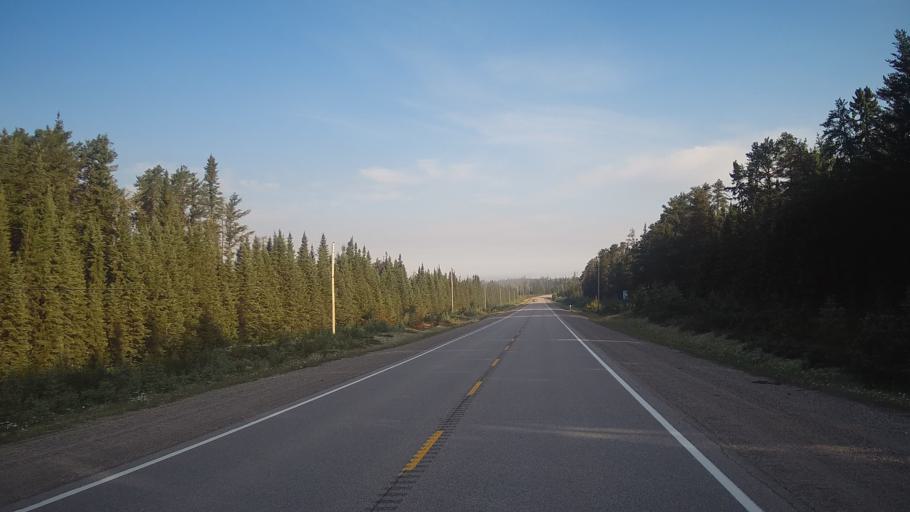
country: CA
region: Ontario
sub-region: Rainy River District
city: Atikokan
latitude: 49.3838
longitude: -91.5912
